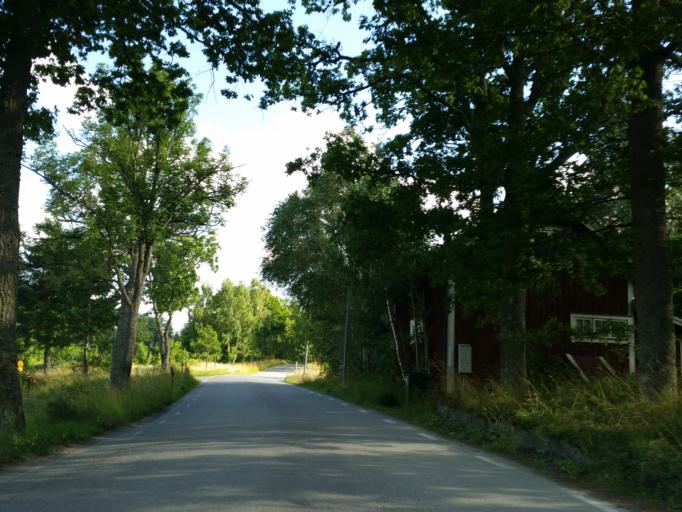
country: SE
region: Soedermanland
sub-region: Strangnas Kommun
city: Mariefred
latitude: 59.2406
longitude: 17.3032
